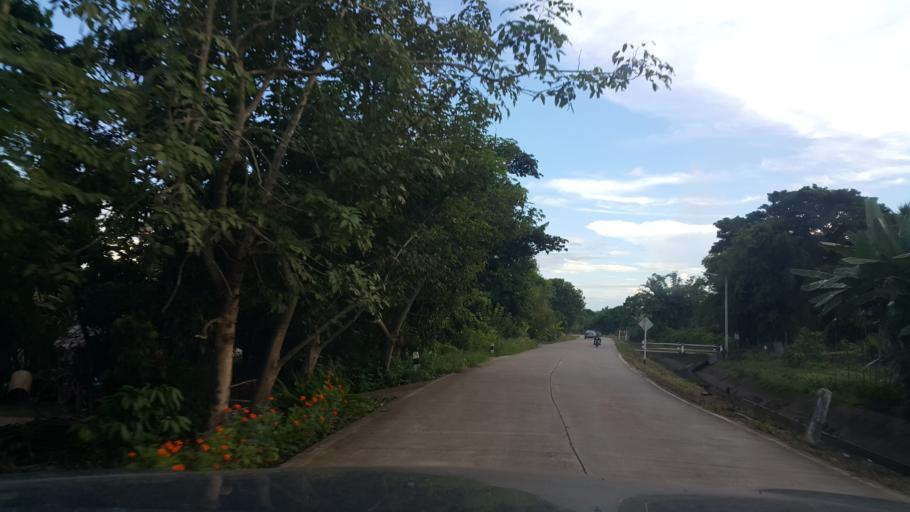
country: TH
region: Chiang Mai
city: Mae Taeng
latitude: 19.1560
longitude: 98.9802
